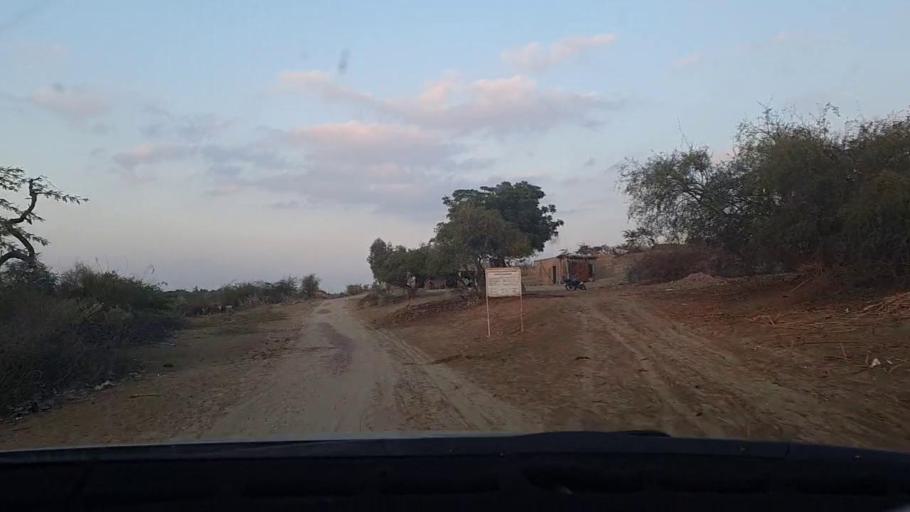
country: PK
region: Sindh
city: Tando Mittha Khan
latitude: 25.9489
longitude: 69.3397
